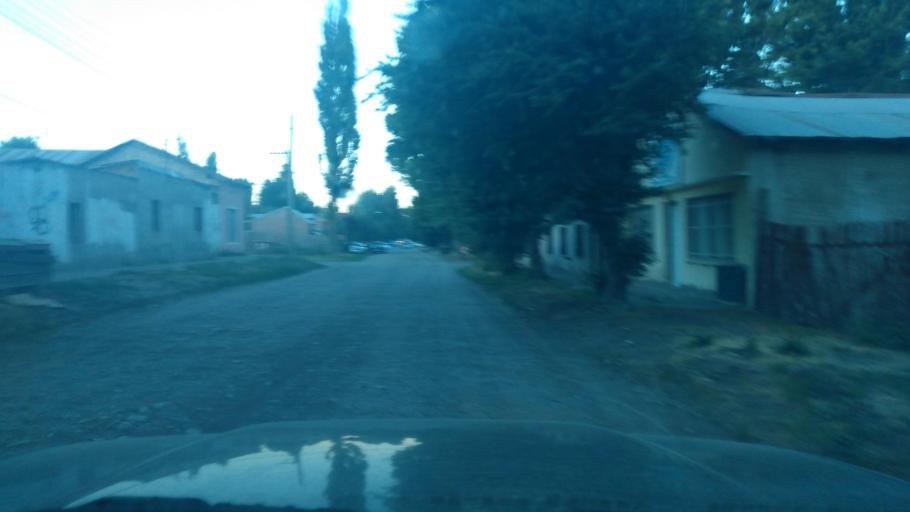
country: AR
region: Neuquen
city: Junin de los Andes
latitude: -39.9535
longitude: -71.0740
